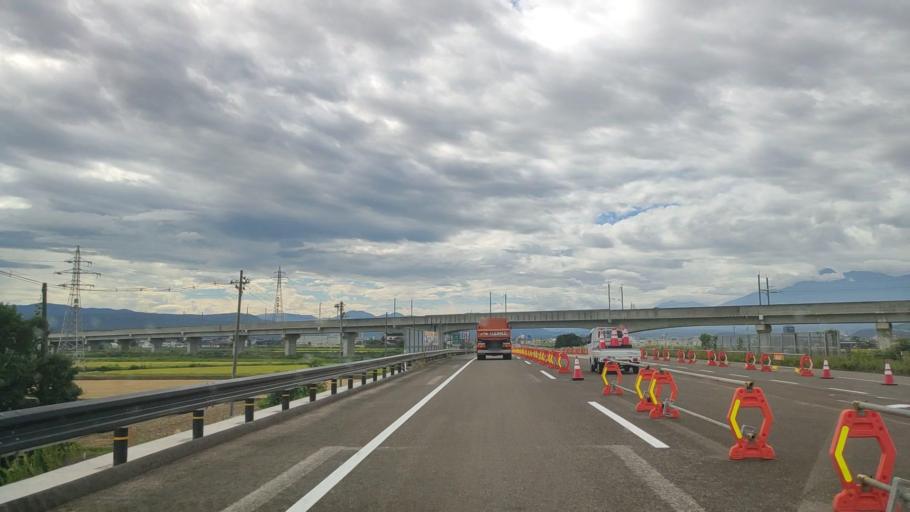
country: JP
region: Niigata
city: Arai
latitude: 37.0698
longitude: 138.2641
